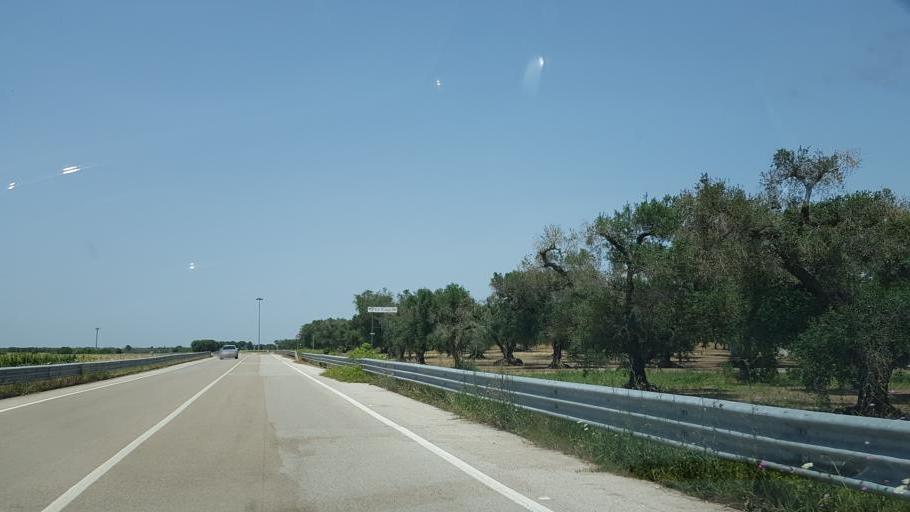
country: IT
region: Apulia
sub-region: Provincia di Brindisi
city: San Pancrazio Salentino
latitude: 40.4833
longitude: 17.8351
